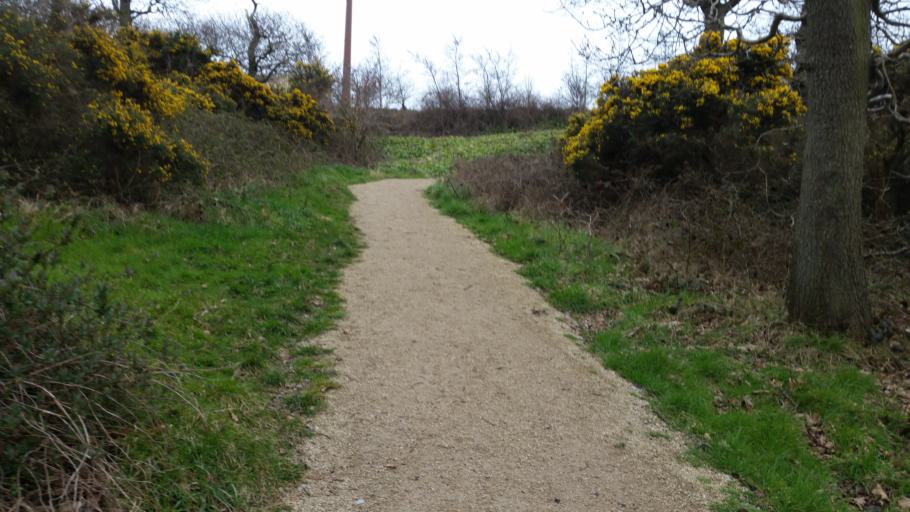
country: IE
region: Leinster
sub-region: Fingal County
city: Howth
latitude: 53.3802
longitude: -6.0696
